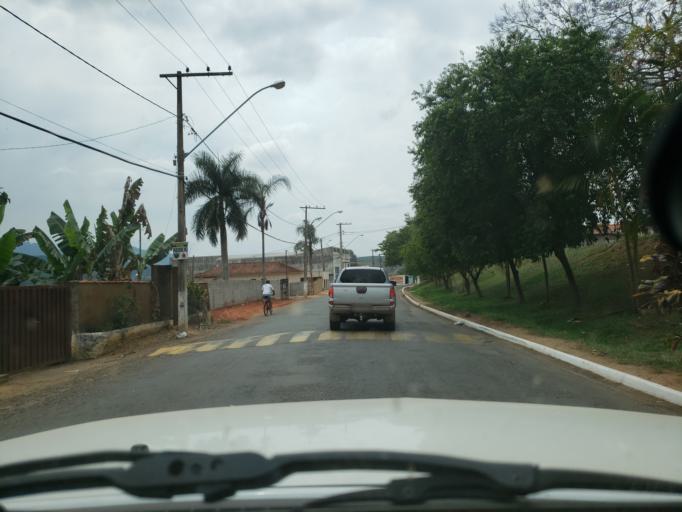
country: BR
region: Minas Gerais
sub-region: Jacutinga
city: Jacutinga
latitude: -22.2773
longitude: -46.6058
